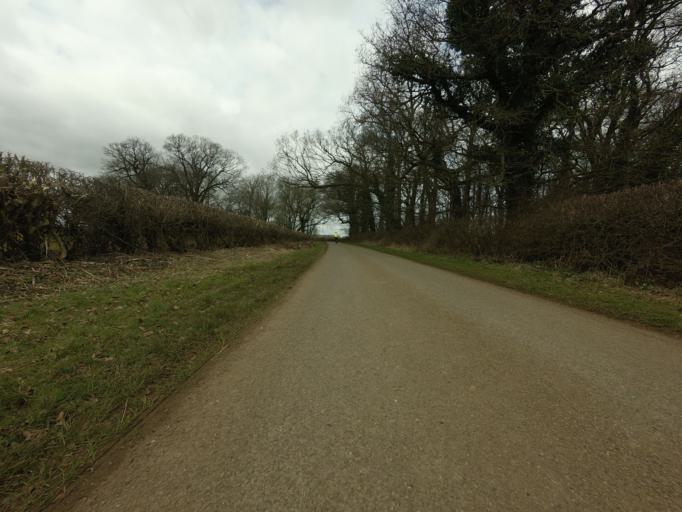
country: GB
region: England
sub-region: Lincolnshire
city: Barrowby
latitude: 52.8701
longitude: -0.6834
